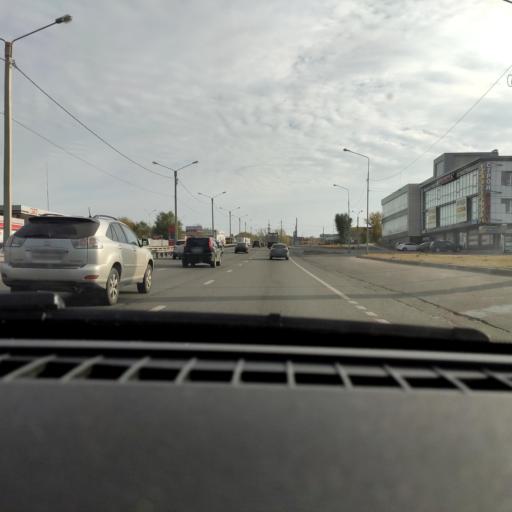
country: RU
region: Voronezj
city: Pridonskoy
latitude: 51.6695
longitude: 39.1232
